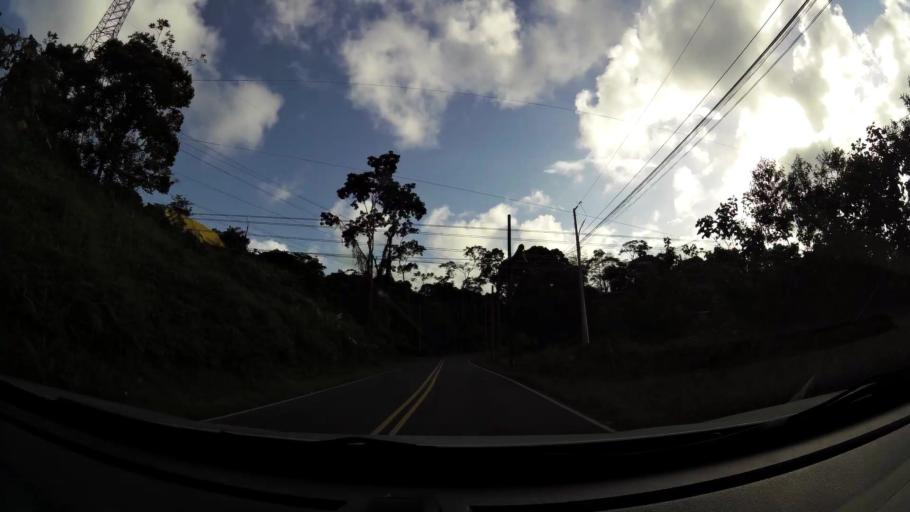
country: CR
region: Limon
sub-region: Canton de Siquirres
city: Siquirres
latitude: 10.0702
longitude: -83.5513
